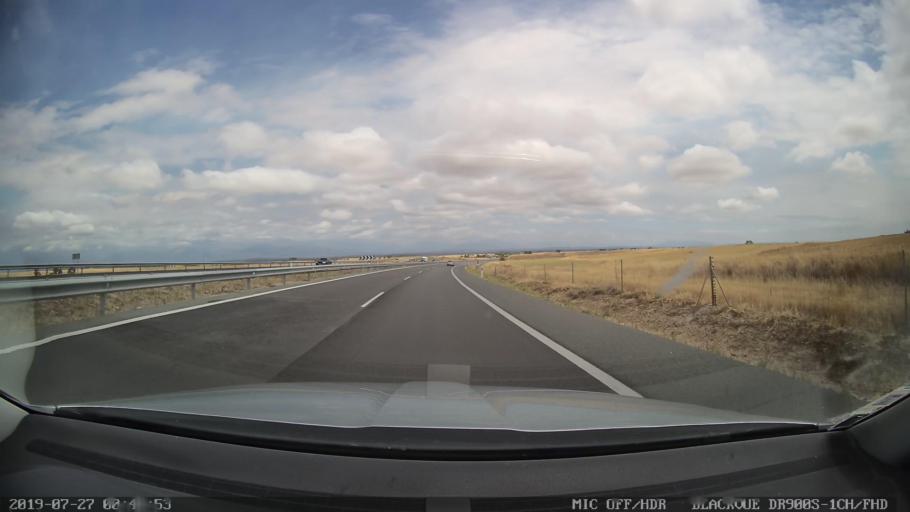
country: ES
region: Castille-La Mancha
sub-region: Province of Toledo
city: Lagartera
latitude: 39.9213
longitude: -5.2055
